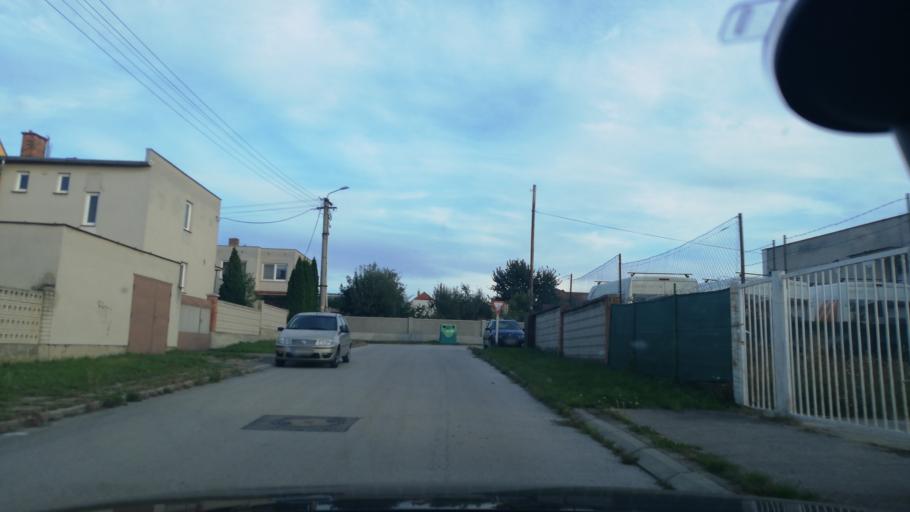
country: SK
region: Trnavsky
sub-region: Okres Skalica
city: Skalica
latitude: 48.8389
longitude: 17.2351
